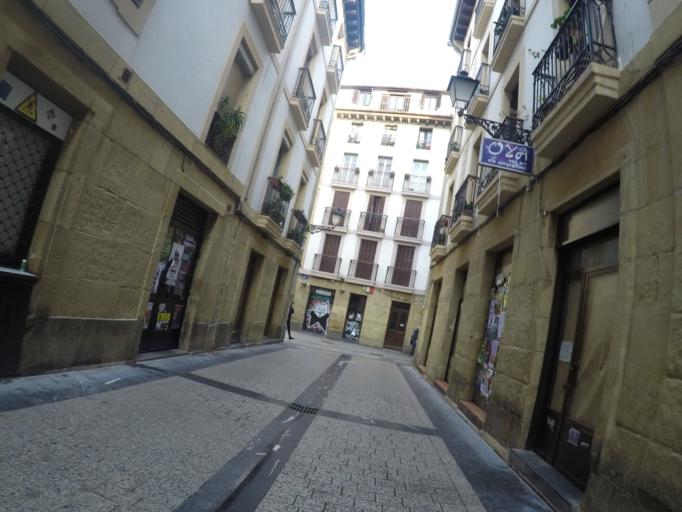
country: ES
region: Basque Country
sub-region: Provincia de Guipuzcoa
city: San Sebastian
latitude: 43.3241
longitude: -1.9846
